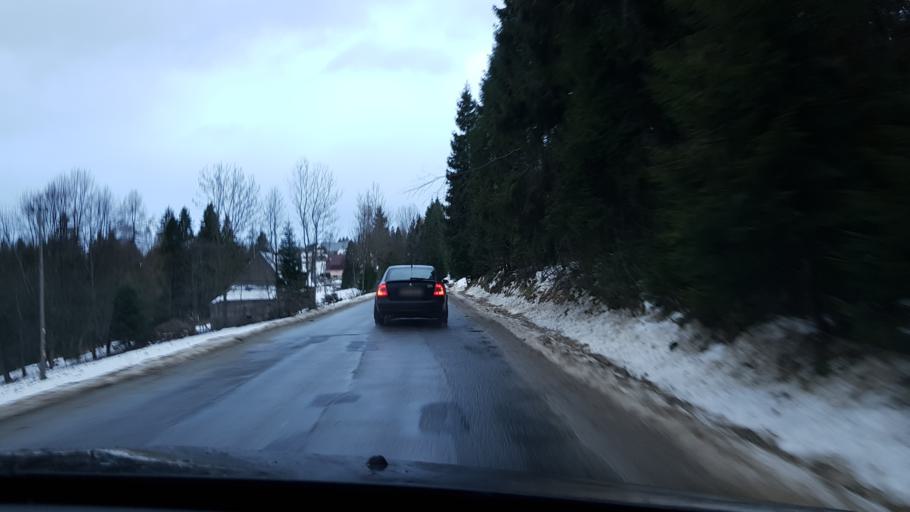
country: PL
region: Lesser Poland Voivodeship
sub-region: Powiat tatrzanski
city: Bukowina Tatrzanska
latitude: 49.3198
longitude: 20.1108
